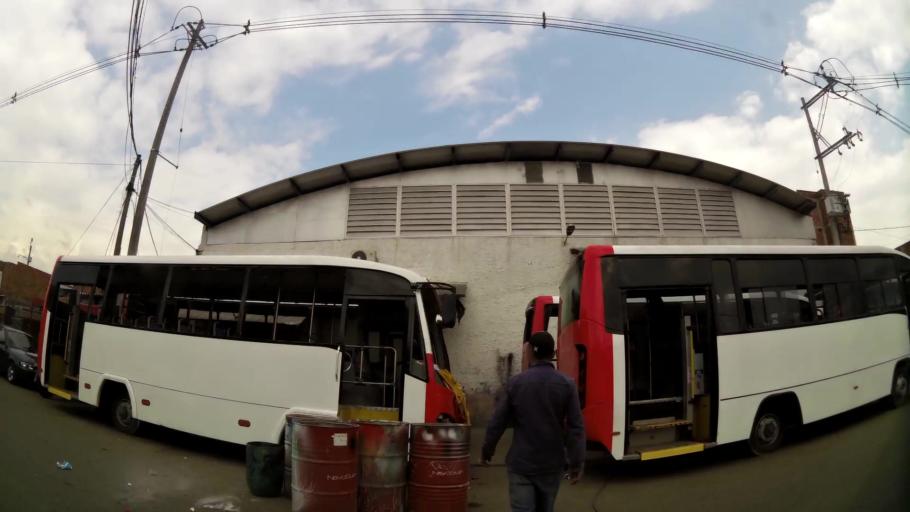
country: CO
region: Antioquia
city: Medellin
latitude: 6.2252
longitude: -75.5872
